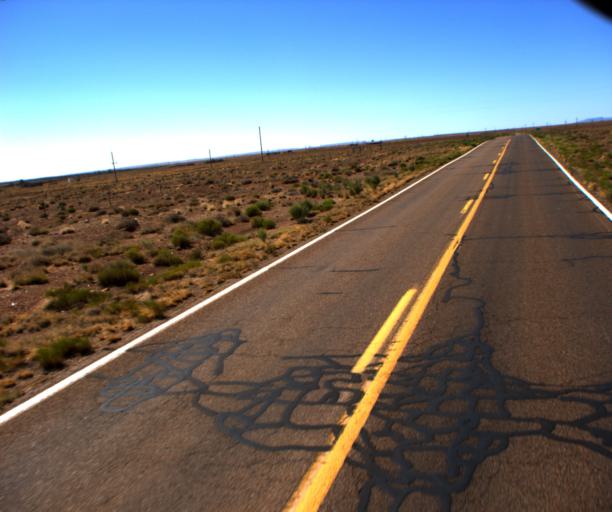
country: US
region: Arizona
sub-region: Coconino County
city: LeChee
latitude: 35.2862
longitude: -110.9839
